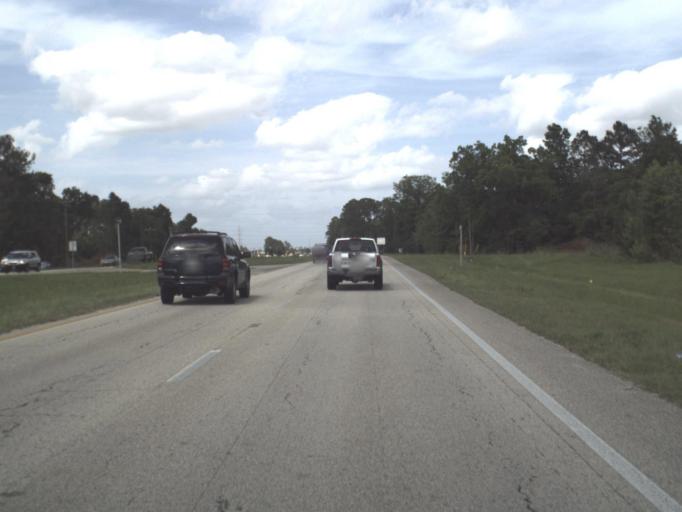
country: US
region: Florida
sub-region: Clay County
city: Middleburg
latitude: 30.0992
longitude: -81.8367
